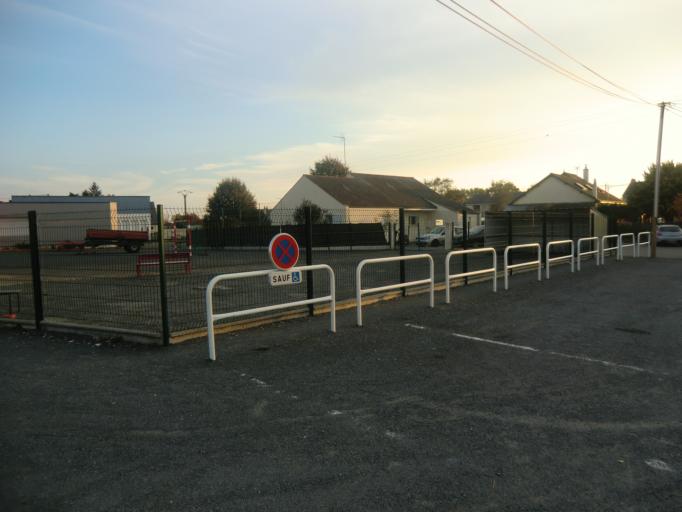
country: FR
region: Pays de la Loire
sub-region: Departement de Maine-et-Loire
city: Vivy
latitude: 47.3283
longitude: -0.0599
